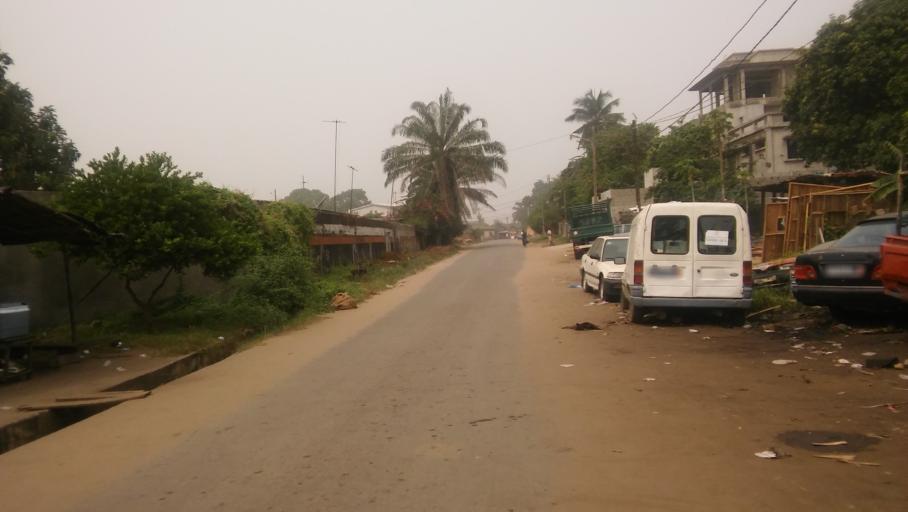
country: CI
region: Sud-Comoe
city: Grand-Bassam
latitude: 5.2120
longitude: -3.7316
